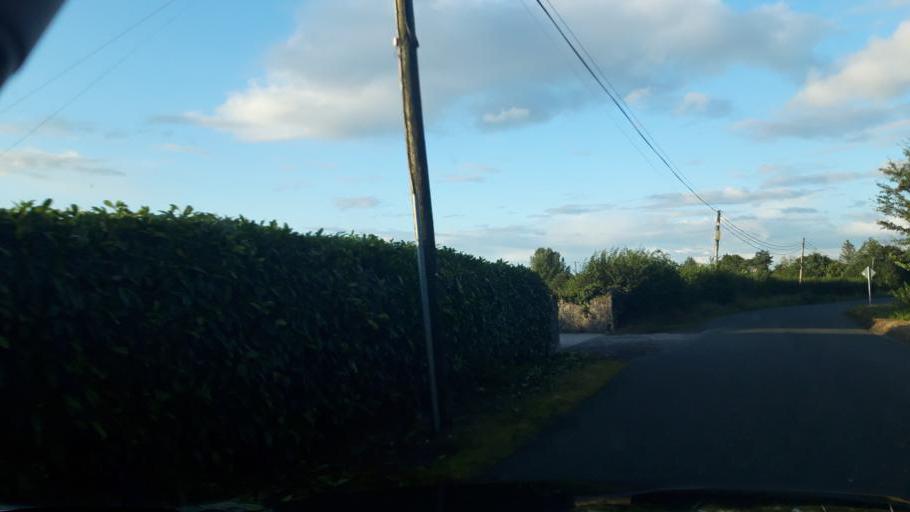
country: IE
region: Leinster
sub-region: An Iarmhi
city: Athlone
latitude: 53.4343
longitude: -7.8701
